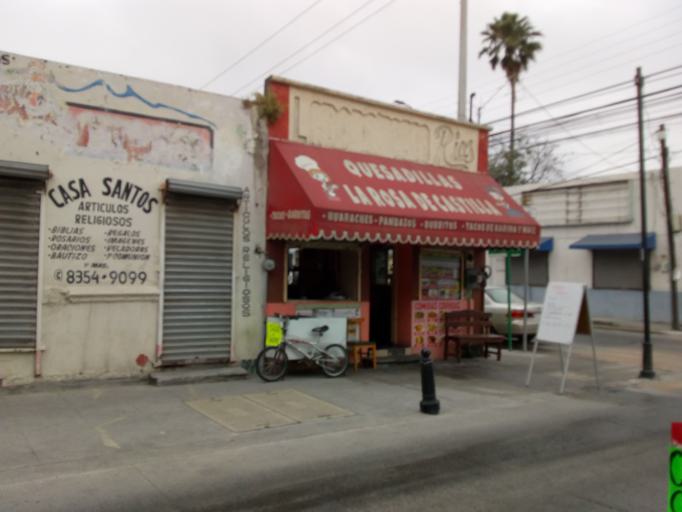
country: MX
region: Nuevo Leon
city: Guadalupe
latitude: 25.6788
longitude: -100.2597
